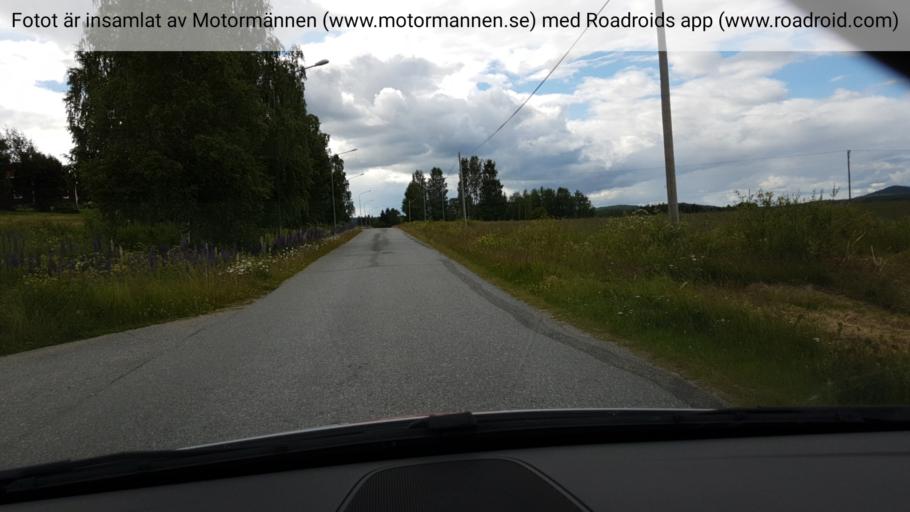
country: SE
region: Vaesterbotten
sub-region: Dorotea Kommun
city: Dorotea
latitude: 63.9130
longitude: 16.3037
